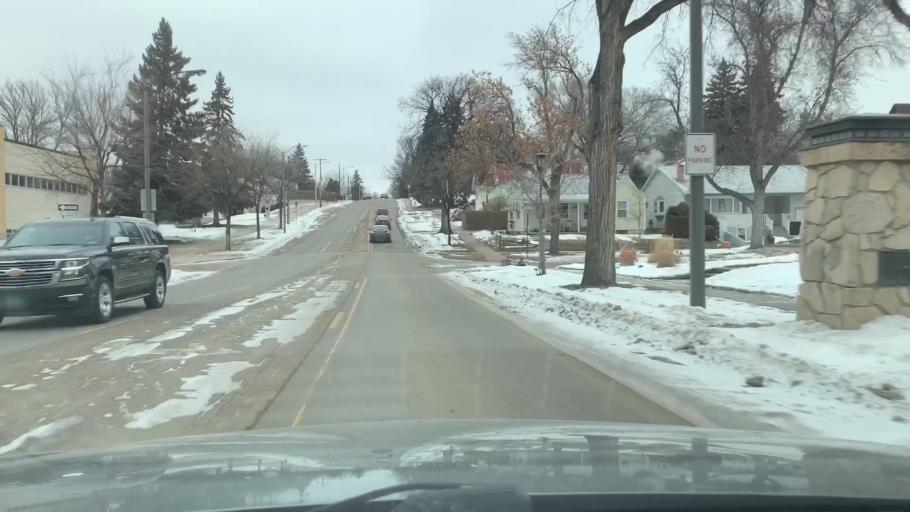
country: US
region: North Dakota
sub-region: Burleigh County
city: Bismarck
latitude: 46.8125
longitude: -100.7943
